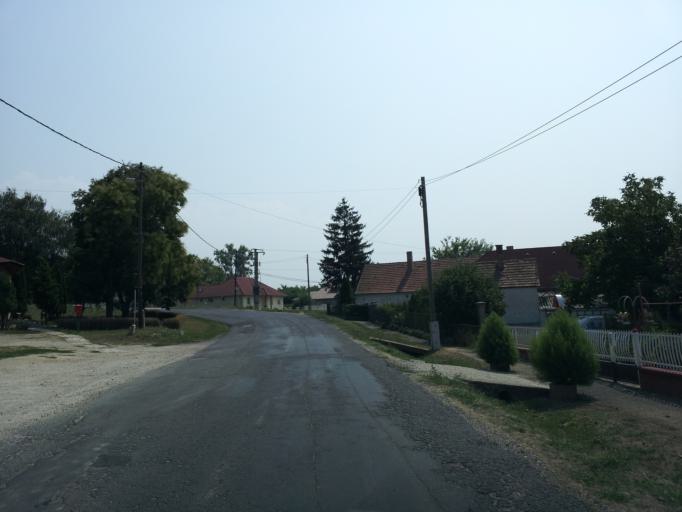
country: HU
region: Gyor-Moson-Sopron
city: Pannonhalma
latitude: 47.5042
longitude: 17.7877
